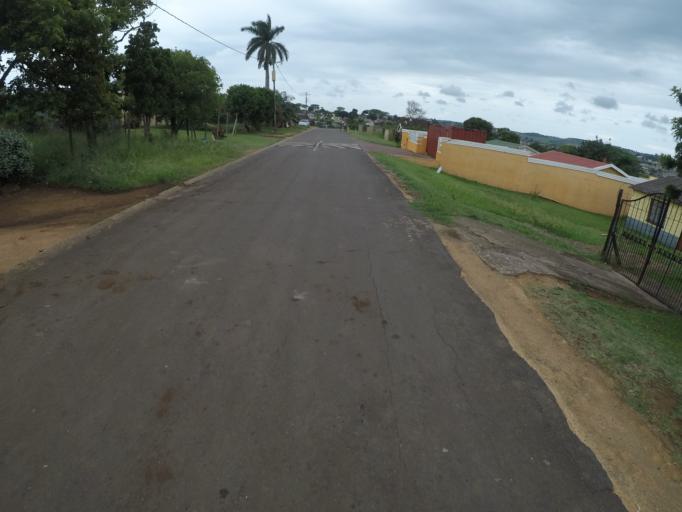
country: ZA
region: KwaZulu-Natal
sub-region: uThungulu District Municipality
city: Empangeni
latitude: -28.7739
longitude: 31.8559
